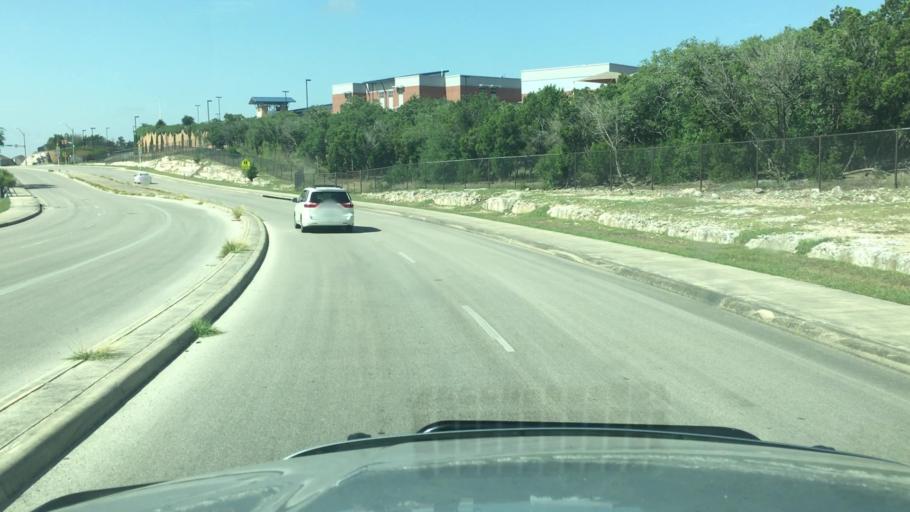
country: US
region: Texas
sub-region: Bexar County
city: Timberwood Park
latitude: 29.6746
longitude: -98.4544
